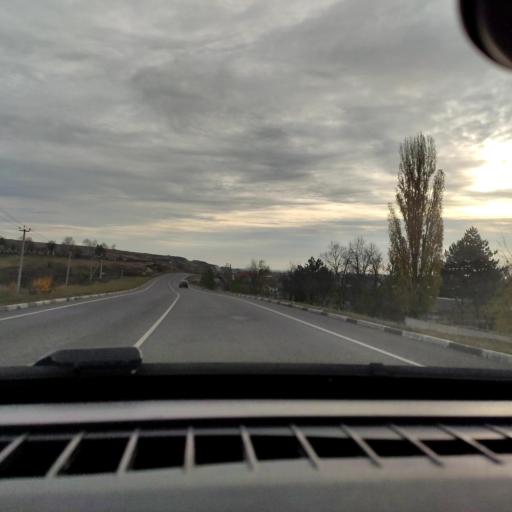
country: RU
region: Belgorod
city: Alekseyevka
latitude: 50.6427
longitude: 38.6512
